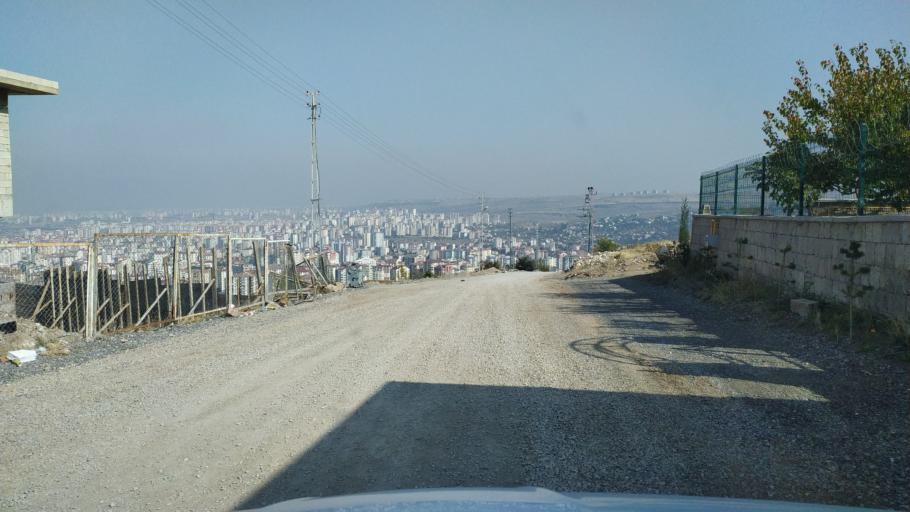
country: TR
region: Kayseri
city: Talas
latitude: 38.6771
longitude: 35.5412
